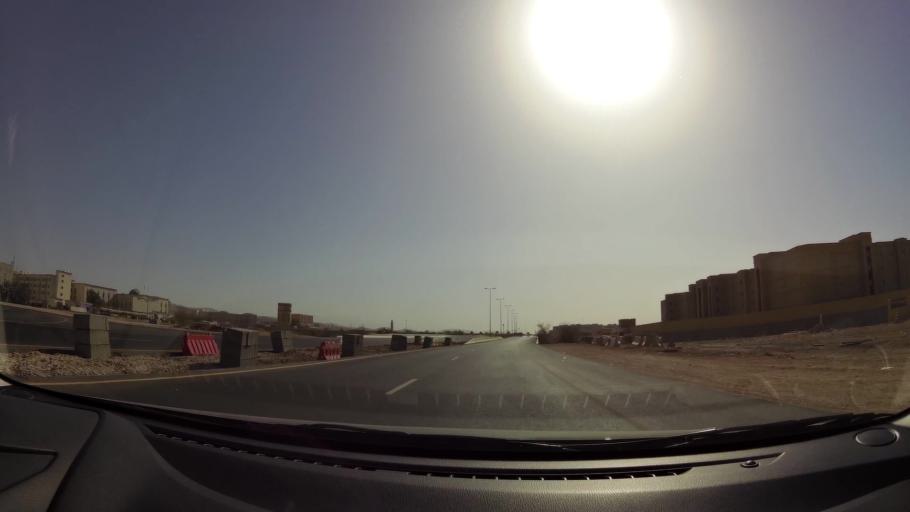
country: OM
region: Muhafazat Masqat
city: Bawshar
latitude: 23.5736
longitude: 58.2854
